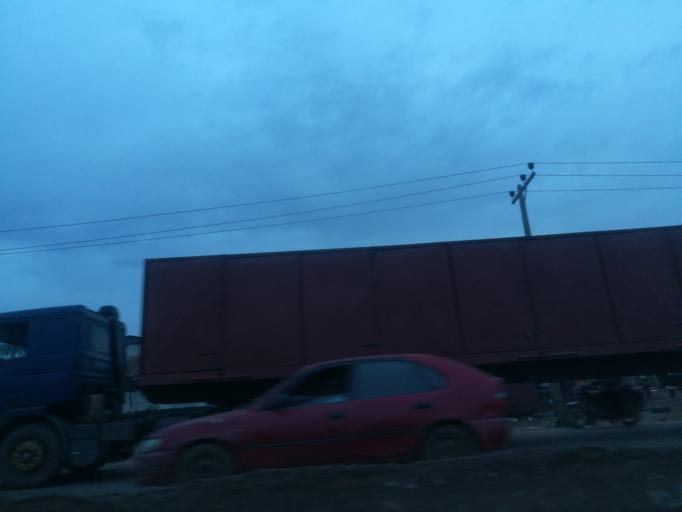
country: NG
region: Oyo
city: Ibadan
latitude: 7.4001
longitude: 3.9482
